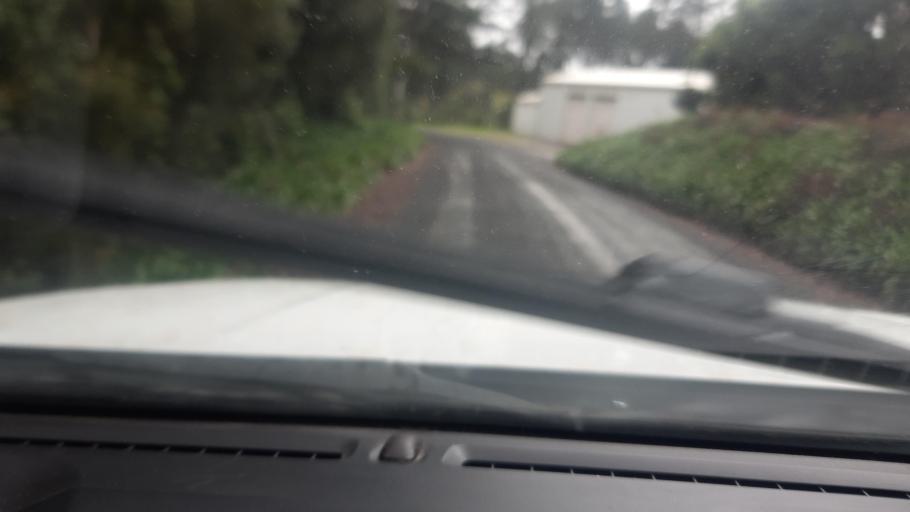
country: NZ
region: Northland
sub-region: Far North District
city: Kaitaia
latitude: -34.9847
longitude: 173.2064
